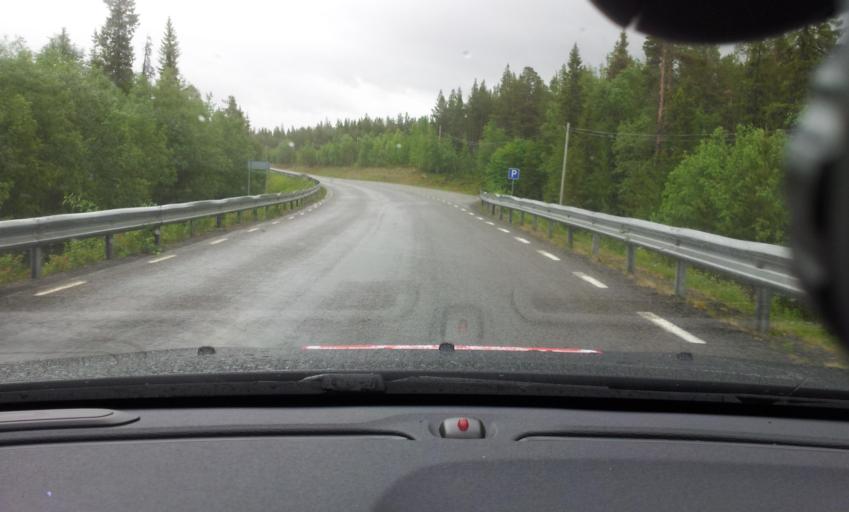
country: SE
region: Jaemtland
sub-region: Are Kommun
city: Are
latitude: 63.1675
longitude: 13.0716
